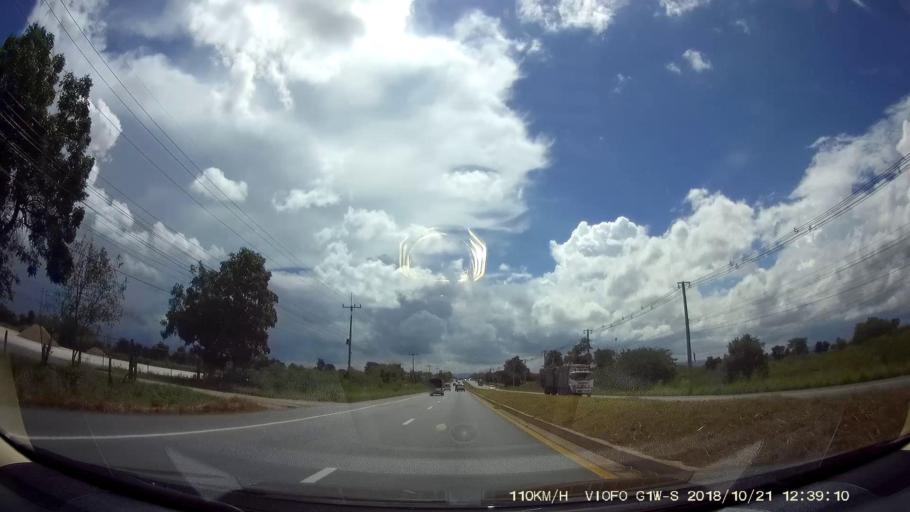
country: TH
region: Nakhon Ratchasima
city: Amphoe Sikhiu
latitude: 15.0424
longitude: 101.7020
